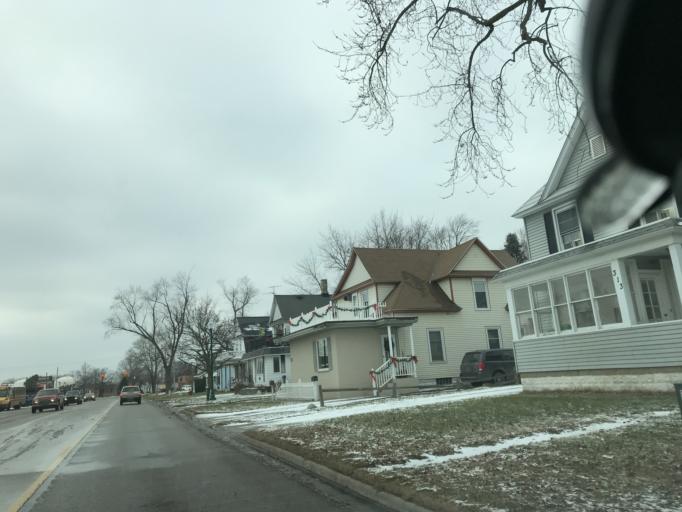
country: US
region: Michigan
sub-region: Ottawa County
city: Zeeland
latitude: 42.8139
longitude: -86.0268
